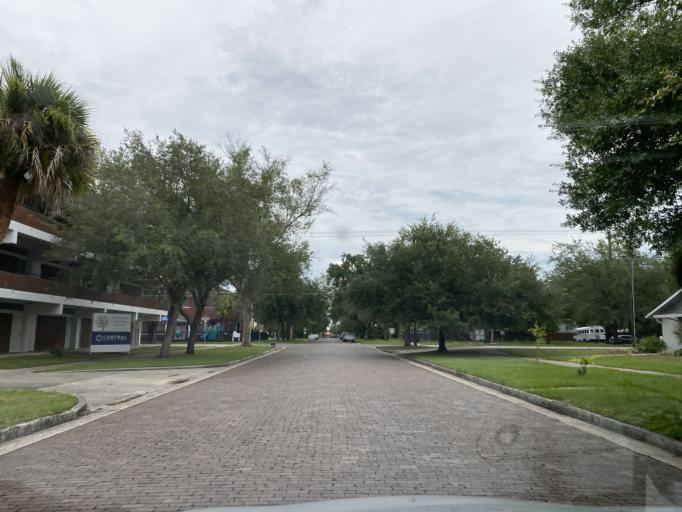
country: US
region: Florida
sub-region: Seminole County
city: Sanford
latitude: 28.8075
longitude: -81.2669
